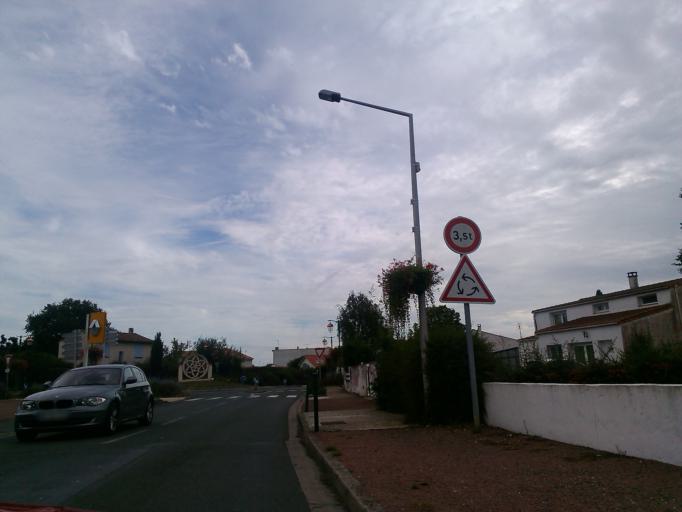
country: FR
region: Poitou-Charentes
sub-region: Departement de la Charente-Maritime
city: Breuillet
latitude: 45.6953
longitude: -1.0511
